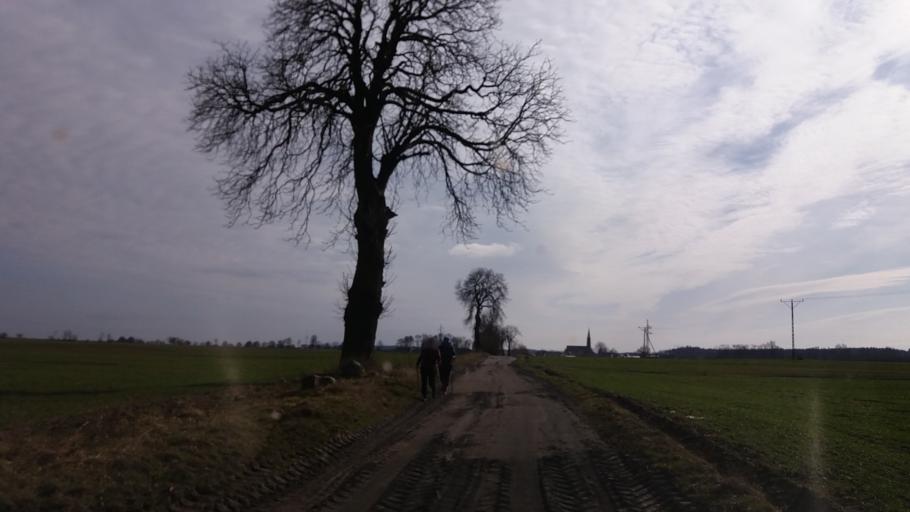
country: PL
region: West Pomeranian Voivodeship
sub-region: Powiat choszczenski
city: Krzecin
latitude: 53.1502
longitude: 15.5015
